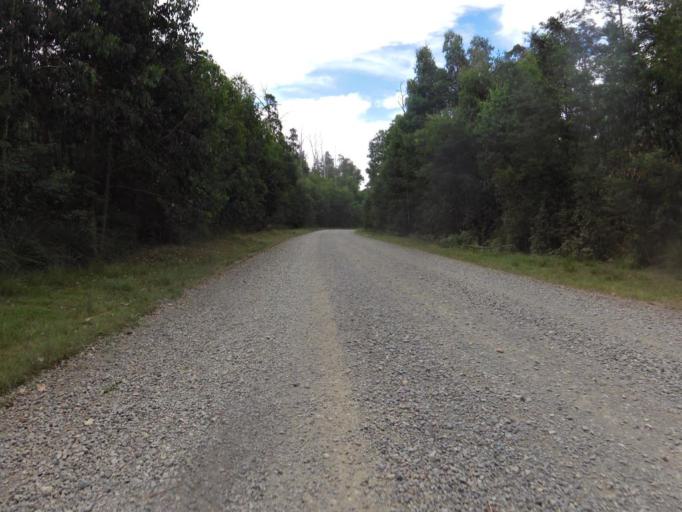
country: AU
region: Victoria
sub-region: Yarra Ranges
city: Healesville
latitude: -37.3997
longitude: 145.5593
